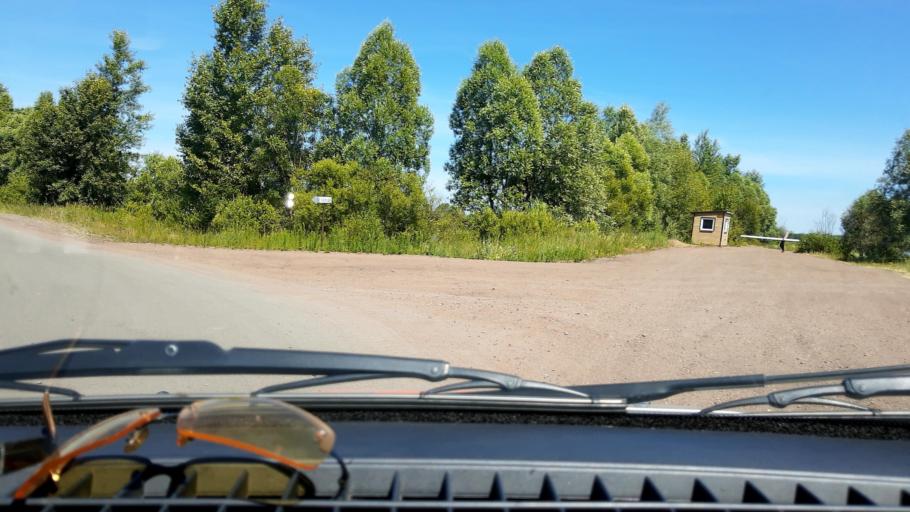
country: RU
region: Bashkortostan
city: Blagoveshchensk
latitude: 54.9662
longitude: 55.8130
